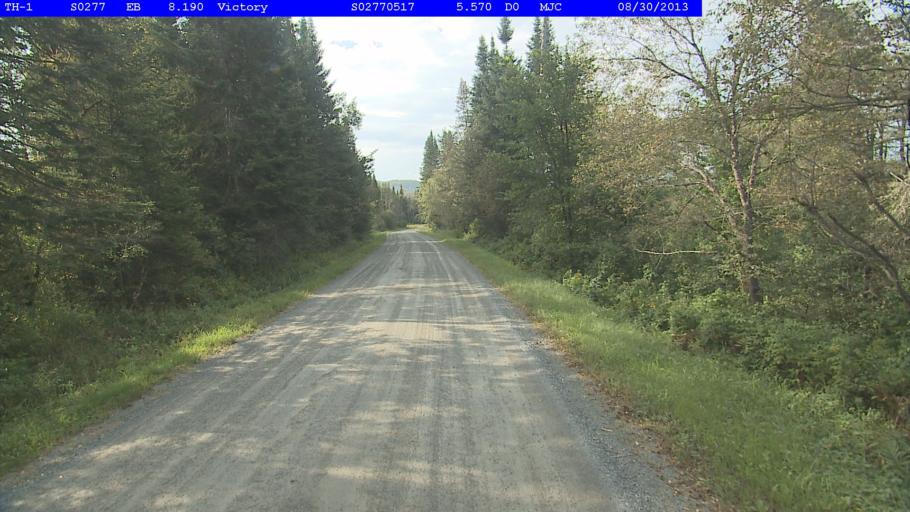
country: US
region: Vermont
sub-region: Caledonia County
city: Lyndonville
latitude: 44.5491
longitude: -71.7859
